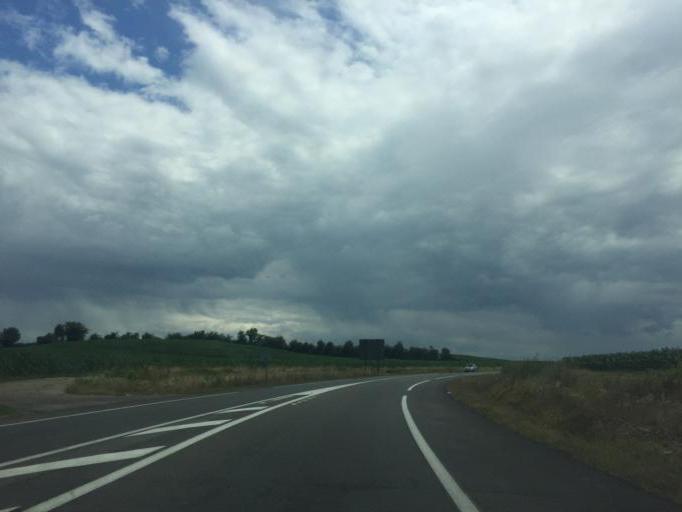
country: FR
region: Rhone-Alpes
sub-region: Departement de l'Isere
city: Janneyrias
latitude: 45.7669
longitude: 5.1192
